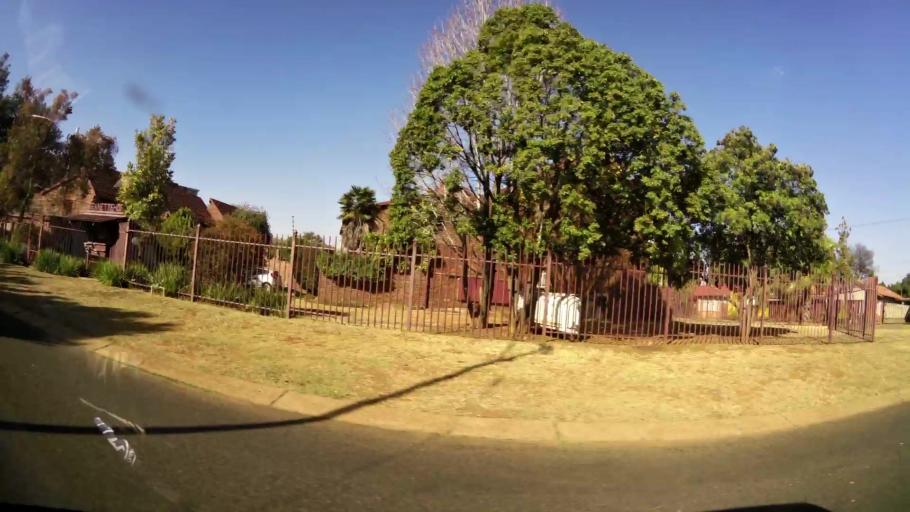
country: ZA
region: Gauteng
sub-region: City of Tshwane Metropolitan Municipality
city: Pretoria
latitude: -25.7228
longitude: 28.2610
